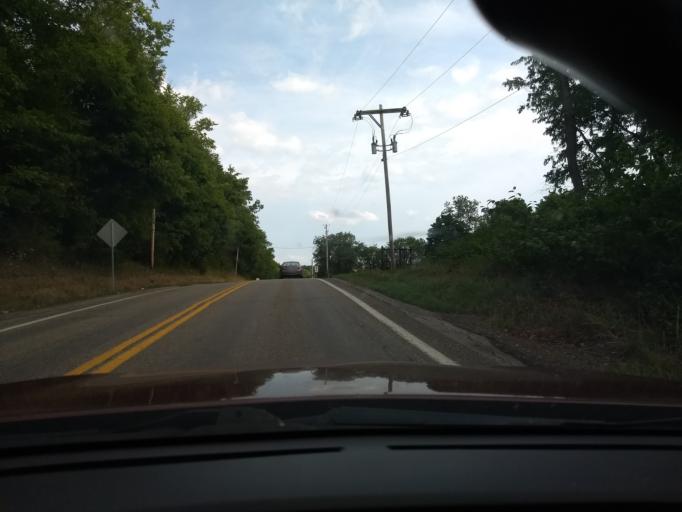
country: US
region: Pennsylvania
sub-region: Allegheny County
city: Curtisville
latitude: 40.6519
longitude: -79.8385
